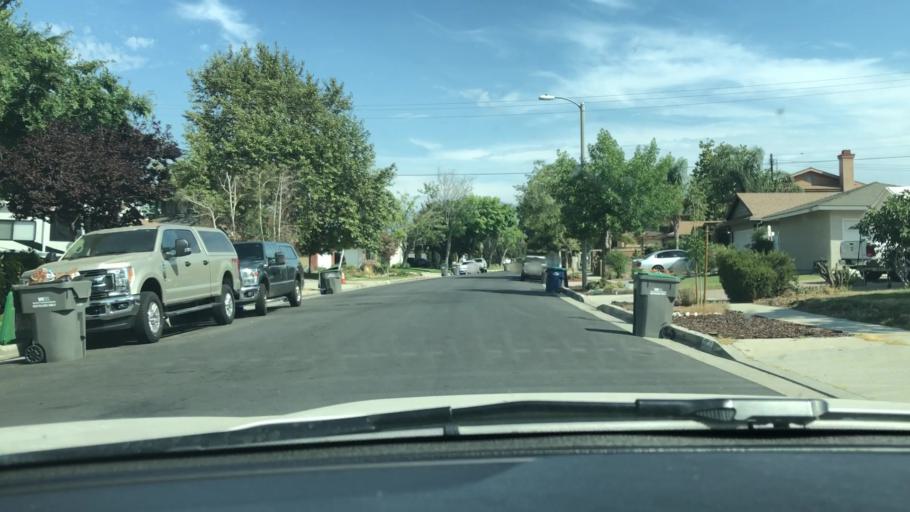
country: US
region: California
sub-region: Los Angeles County
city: Santa Clarita
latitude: 34.4250
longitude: -118.4858
